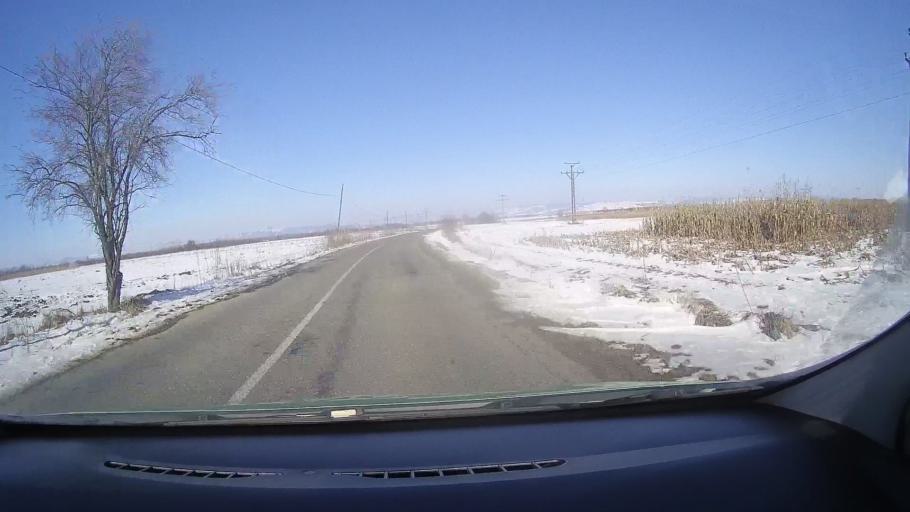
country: RO
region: Brasov
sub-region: Comuna Harseni
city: Harseni
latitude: 45.7664
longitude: 25.0042
